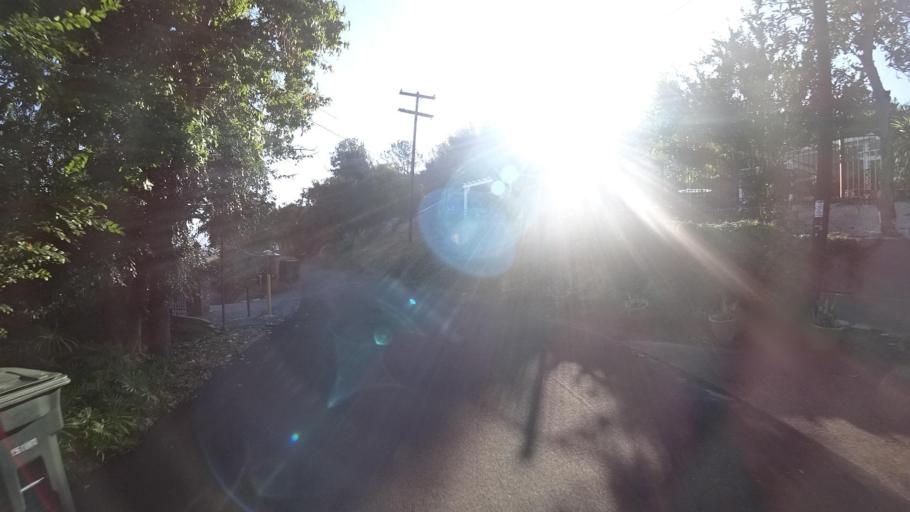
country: US
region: California
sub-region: San Diego County
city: Casa de Oro-Mount Helix
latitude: 32.7723
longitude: -116.9657
